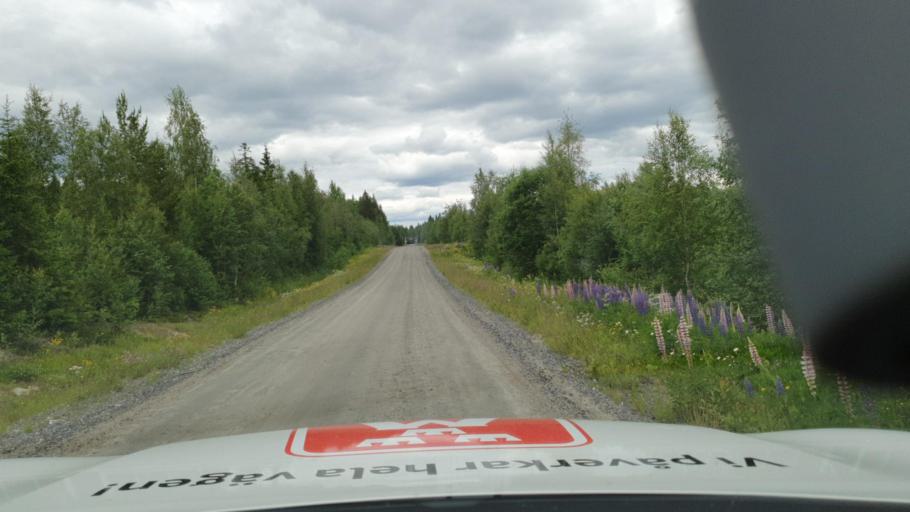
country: SE
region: Vaesterbotten
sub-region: Bjurholms Kommun
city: Bjurholm
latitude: 63.7637
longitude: 19.2619
